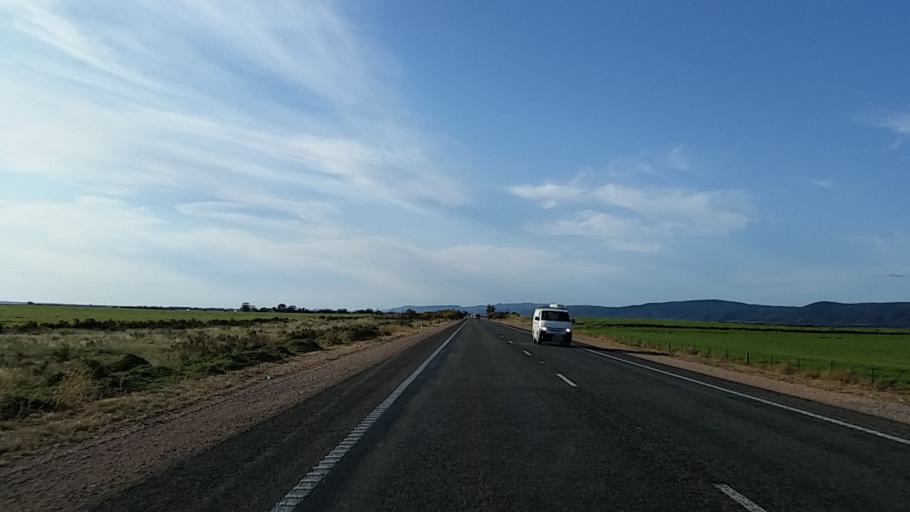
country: AU
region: South Australia
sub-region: Port Pirie City and Dists
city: Port Pirie
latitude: -33.1130
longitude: 138.0683
